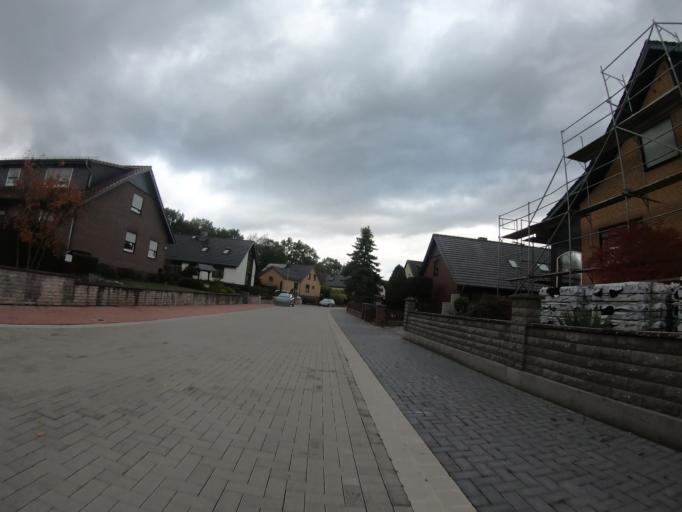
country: DE
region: Lower Saxony
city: Isenbuttel
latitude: 52.4425
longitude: 10.5723
